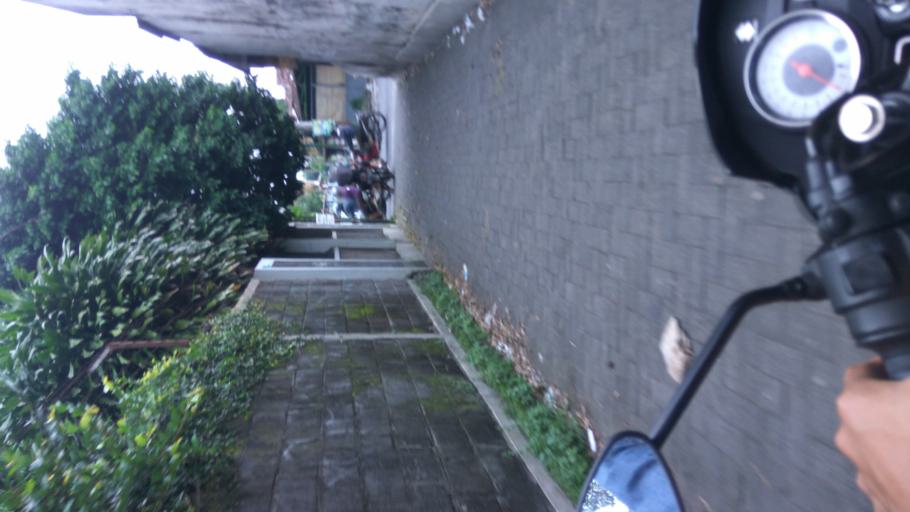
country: ID
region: Daerah Istimewa Yogyakarta
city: Depok
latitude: -7.7551
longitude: 110.4103
